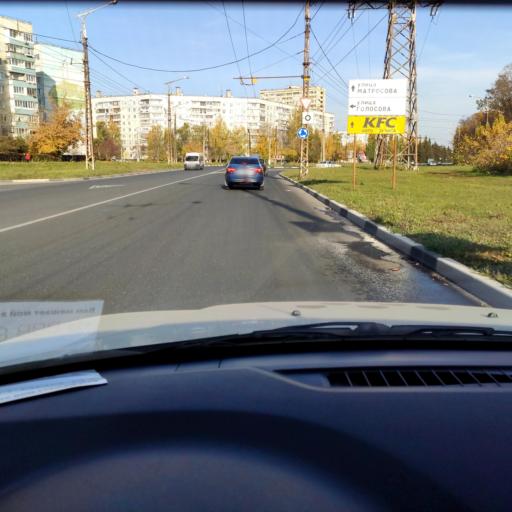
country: RU
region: Samara
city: Tol'yatti
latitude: 53.5040
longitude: 49.4304
